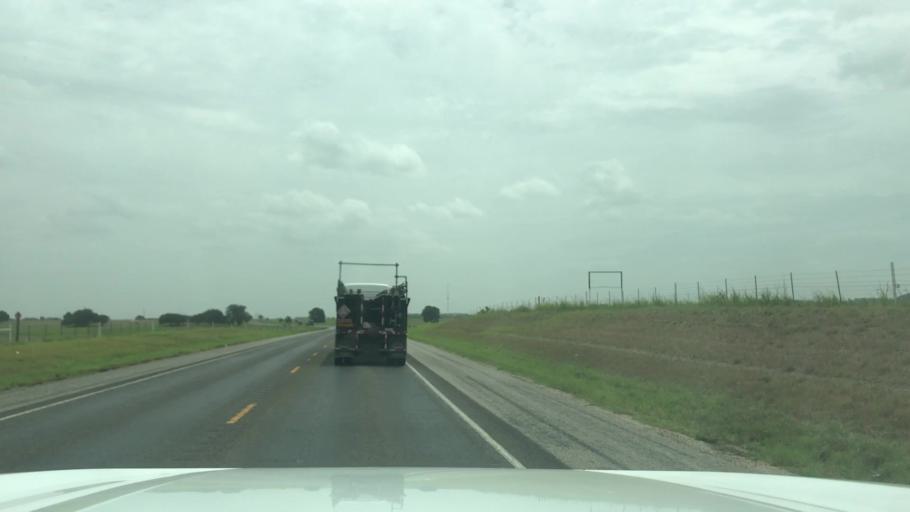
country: US
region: Texas
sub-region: Bosque County
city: Clifton
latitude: 31.8083
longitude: -97.6086
